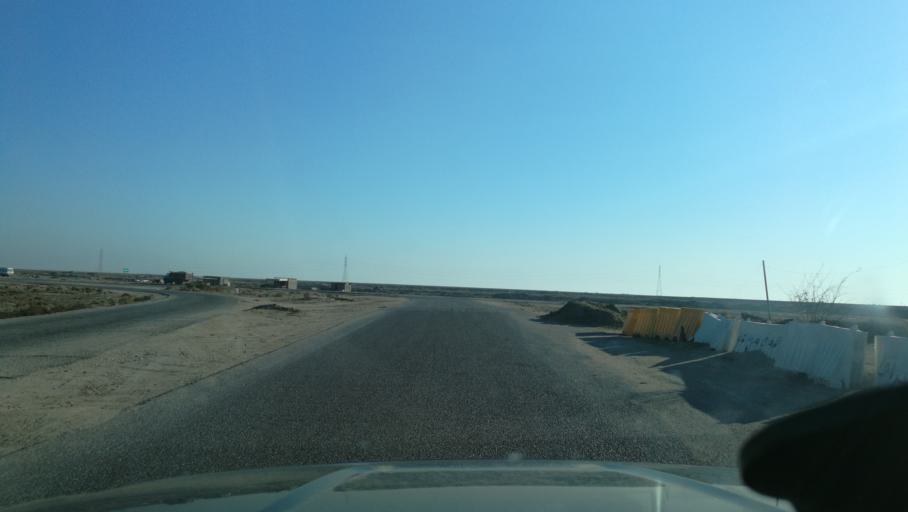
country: IQ
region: Dhi Qar
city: Suq ash Shuyukh
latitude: 30.8037
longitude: 46.3703
